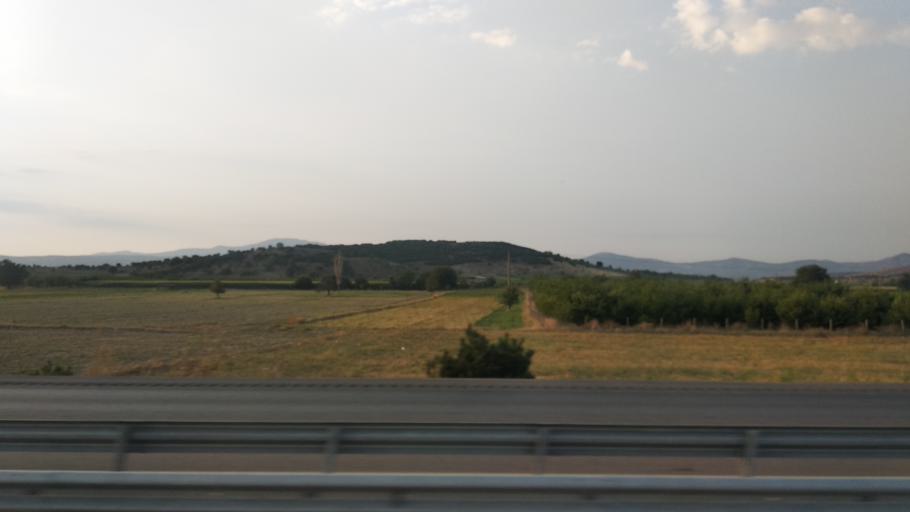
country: TR
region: Manisa
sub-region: Kula
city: Kula
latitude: 38.5538
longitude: 28.6887
